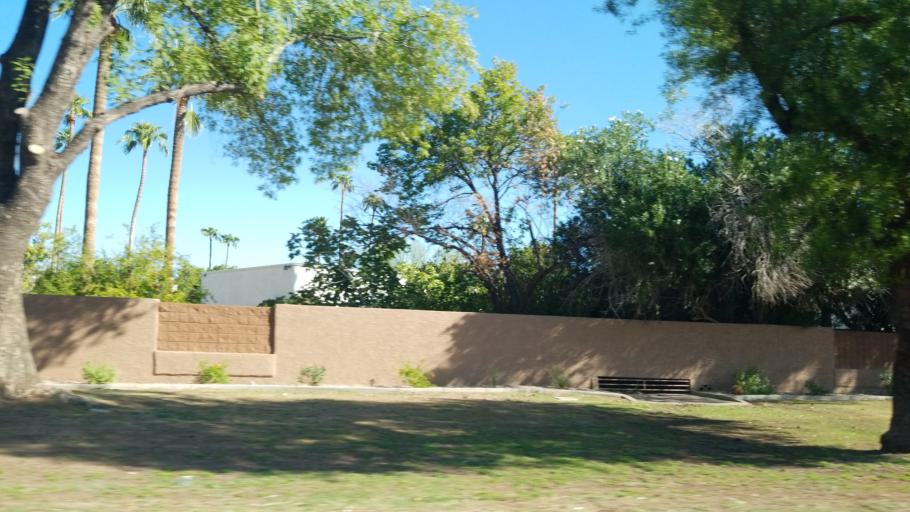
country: US
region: Arizona
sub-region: Maricopa County
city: Scottsdale
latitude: 33.5385
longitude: -111.8946
